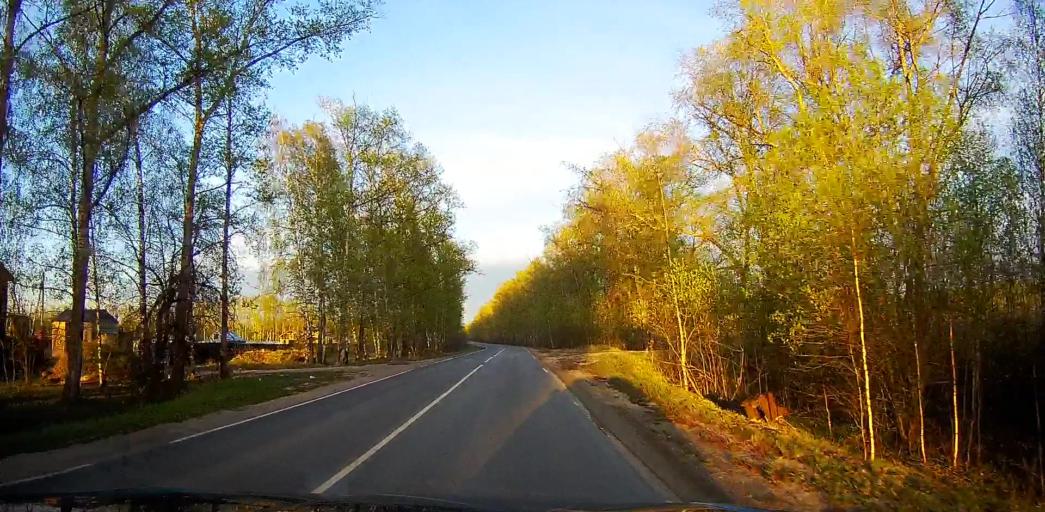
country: RU
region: Moskovskaya
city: Peski
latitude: 55.2092
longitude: 38.7142
